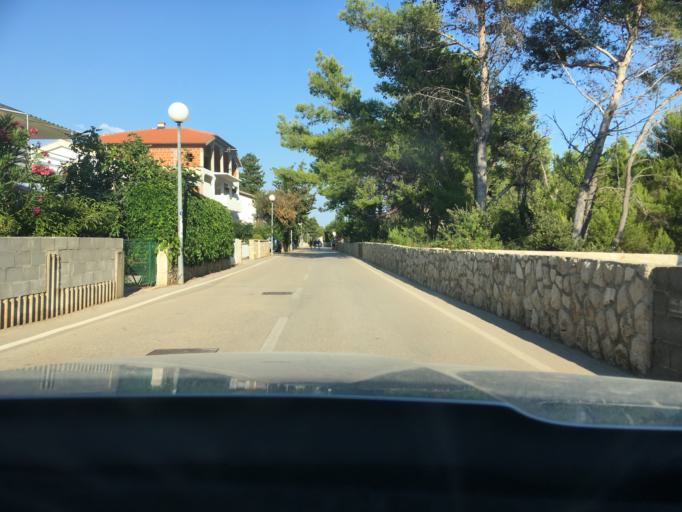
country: HR
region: Zadarska
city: Vir
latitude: 44.2977
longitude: 15.0984
